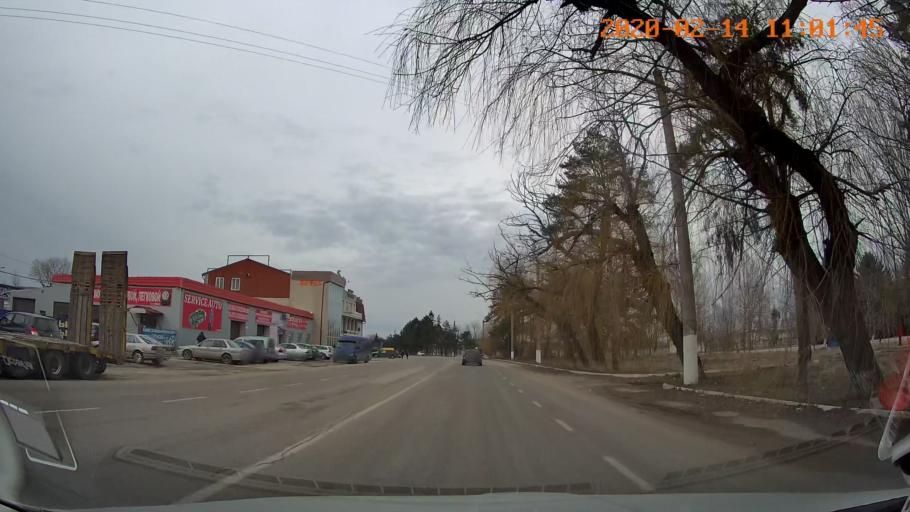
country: MD
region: Raionul Edinet
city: Edinet
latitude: 48.1617
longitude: 27.3263
